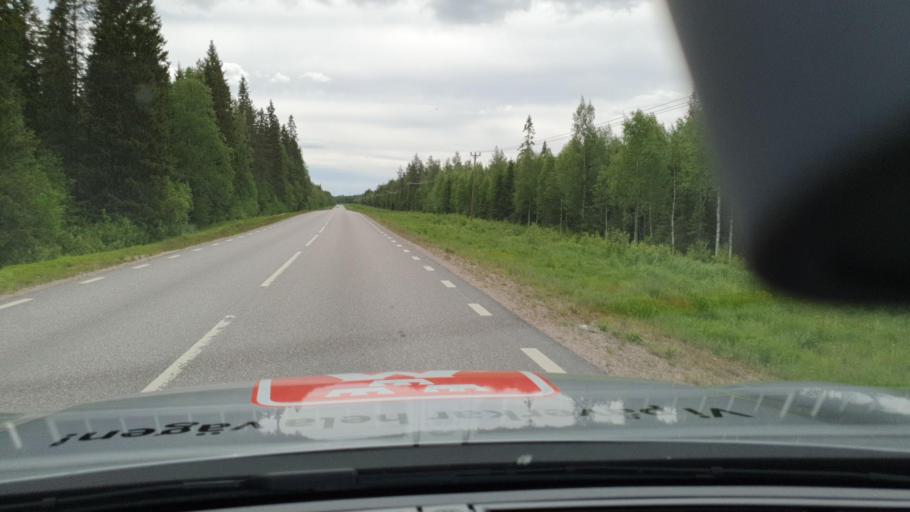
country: SE
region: Norrbotten
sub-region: Kalix Kommun
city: Kalix
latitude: 65.9098
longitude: 23.4552
